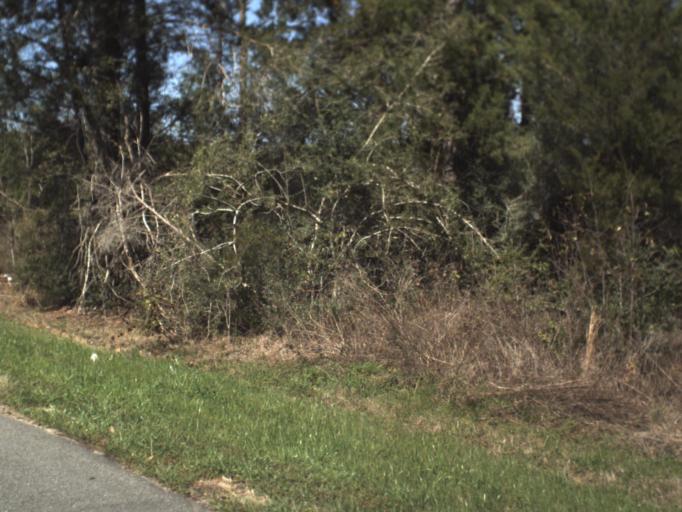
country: US
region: Florida
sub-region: Jackson County
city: Marianna
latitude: 30.7971
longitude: -85.2716
